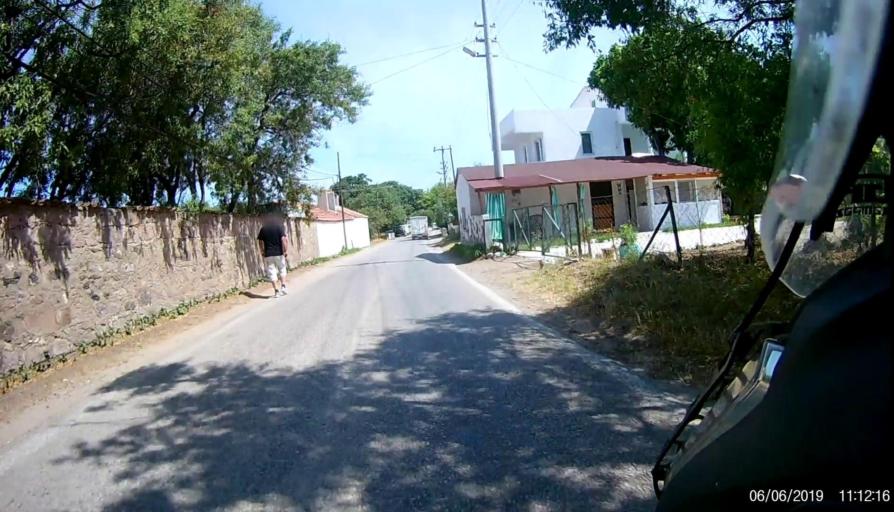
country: TR
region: Canakkale
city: Gulpinar
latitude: 39.6101
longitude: 26.1873
